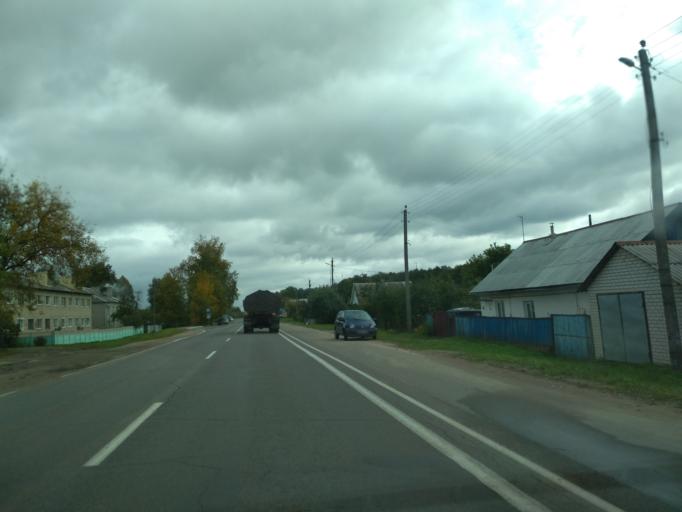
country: BY
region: Minsk
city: Mar''ina Horka
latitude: 53.5243
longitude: 28.1457
